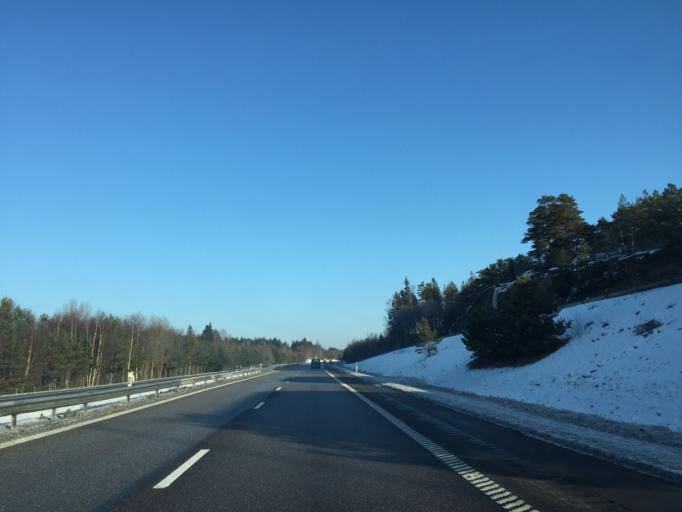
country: SE
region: Vaestra Goetaland
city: Svanesund
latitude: 58.1148
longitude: 11.8798
